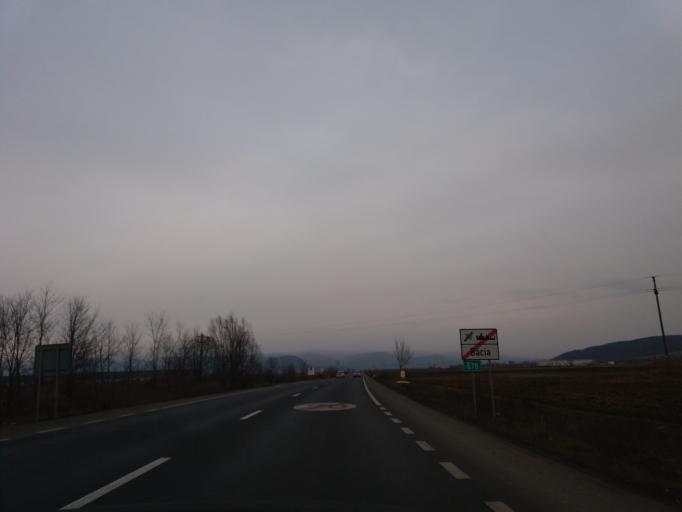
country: RO
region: Hunedoara
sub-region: Comuna Bacia
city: Bacia
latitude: 45.8079
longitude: 23.0148
